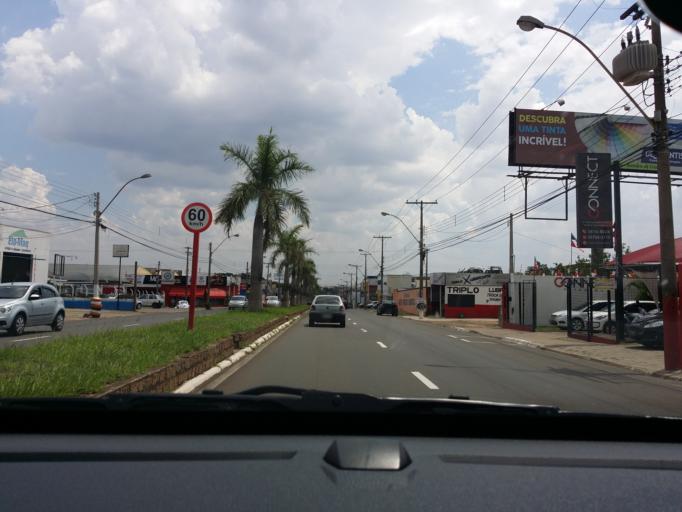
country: BR
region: Sao Paulo
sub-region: Sao Carlos
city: Sao Carlos
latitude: -22.0334
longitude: -47.8810
